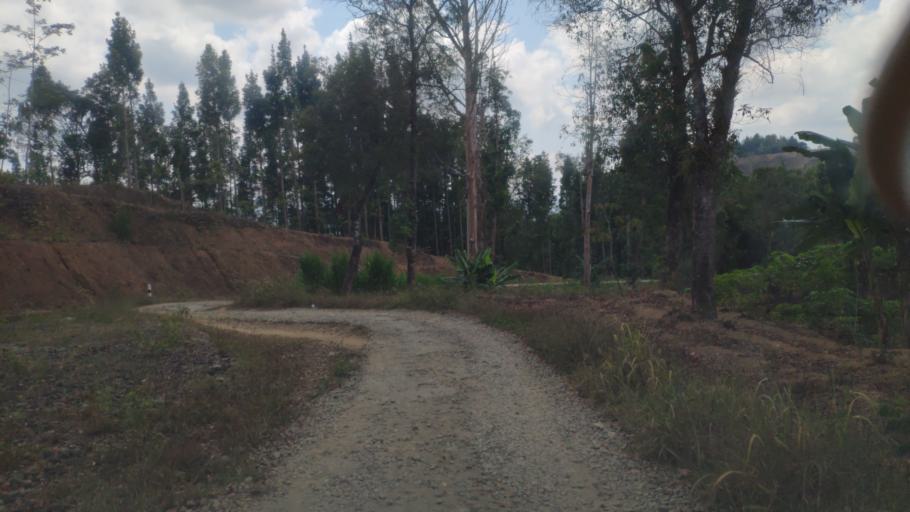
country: ID
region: Central Java
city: Wonosobo
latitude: -7.4717
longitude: 109.7191
